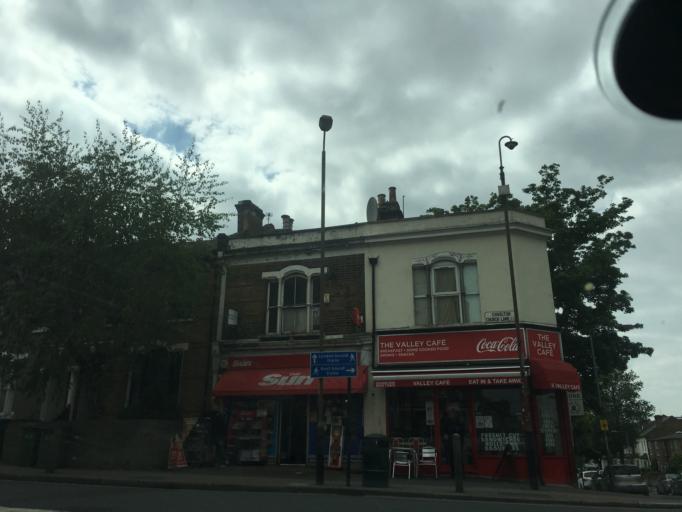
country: GB
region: England
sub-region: Greater London
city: Woolwich
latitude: 51.4865
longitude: 0.0325
